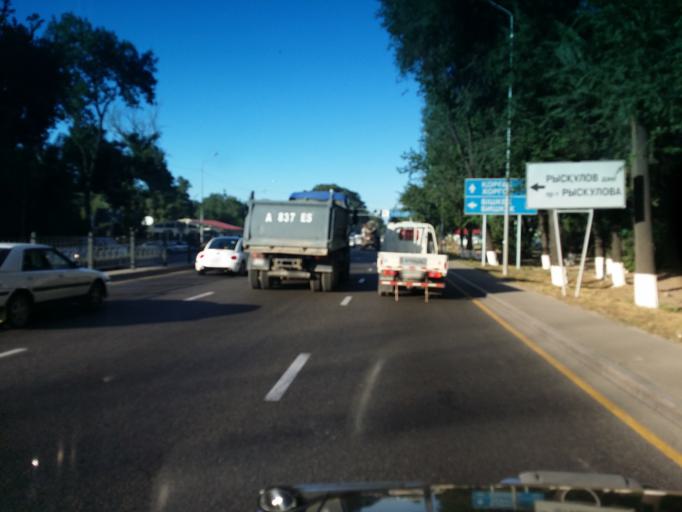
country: KZ
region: Almaty Qalasy
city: Almaty
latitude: 43.2946
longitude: 76.9964
